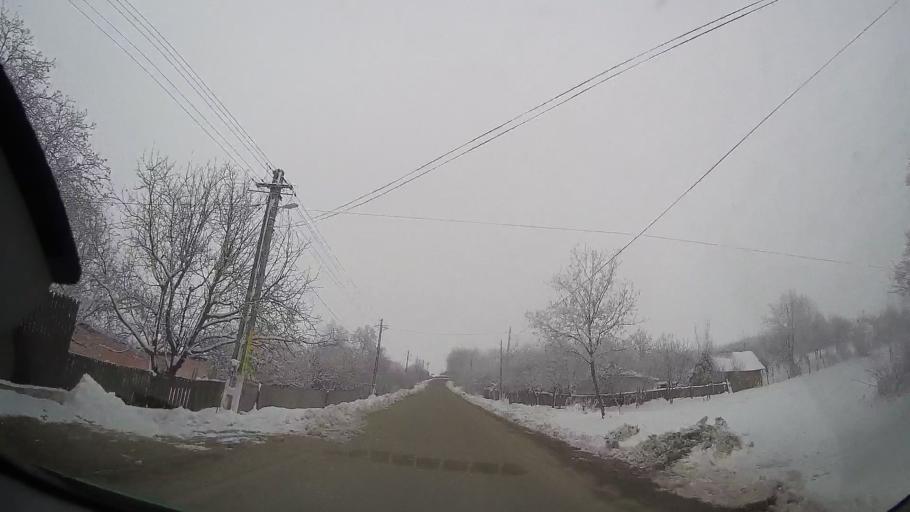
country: RO
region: Neamt
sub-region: Comuna Pancesti
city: Pancesti
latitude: 46.9073
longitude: 27.1569
